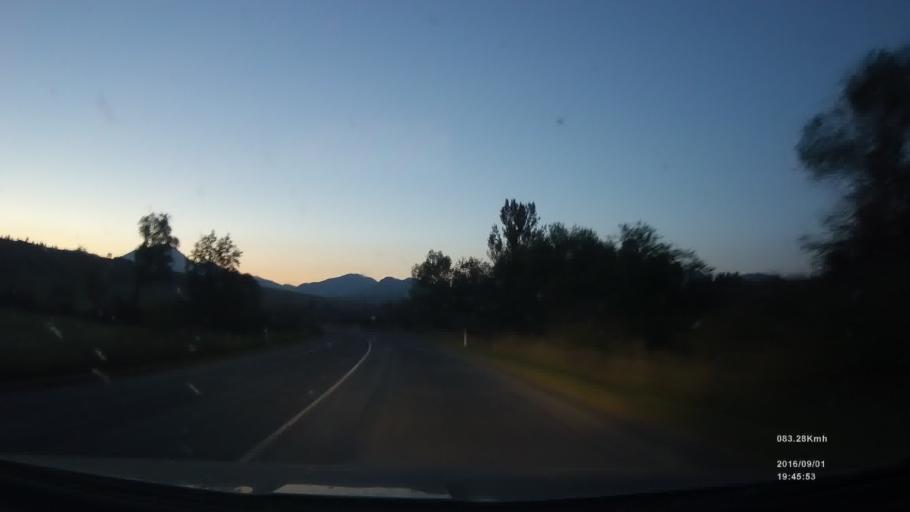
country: SK
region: Zilinsky
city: Ruzomberok
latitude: 49.0840
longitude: 19.4394
